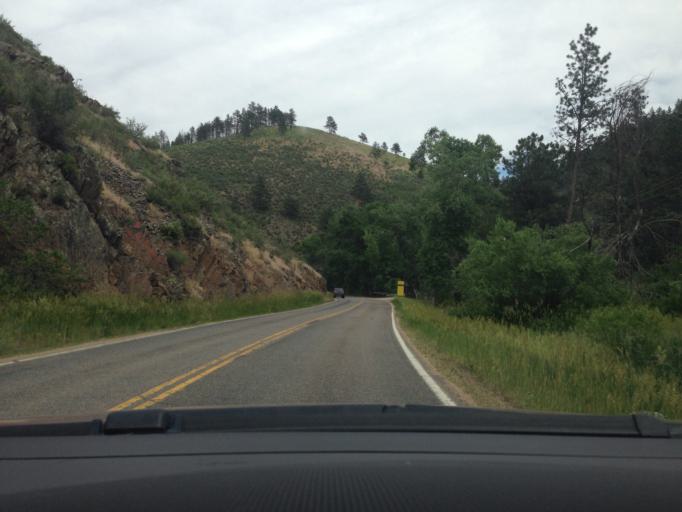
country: US
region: Colorado
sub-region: Larimer County
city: Laporte
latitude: 40.6264
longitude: -105.2209
